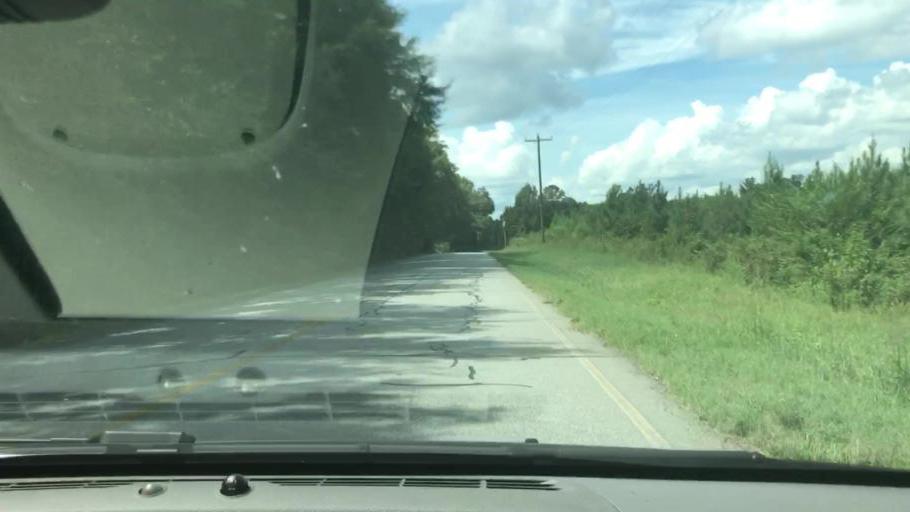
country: US
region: Georgia
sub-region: Stewart County
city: Lumpkin
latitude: 32.1377
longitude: -84.9529
